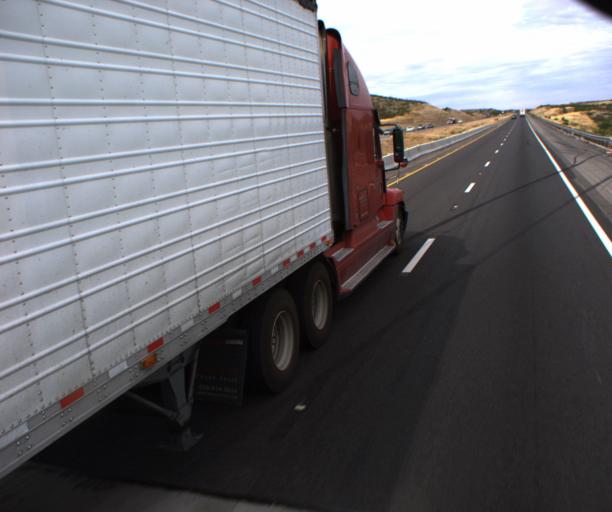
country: US
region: Arizona
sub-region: Cochise County
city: Mescal
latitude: 31.9861
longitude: -110.5678
